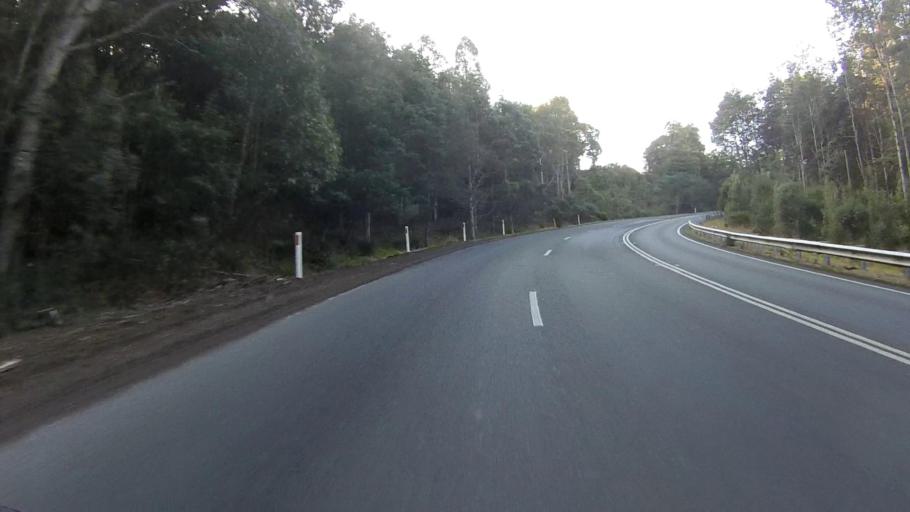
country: AU
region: Tasmania
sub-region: Sorell
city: Sorell
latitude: -42.9957
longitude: 147.9251
